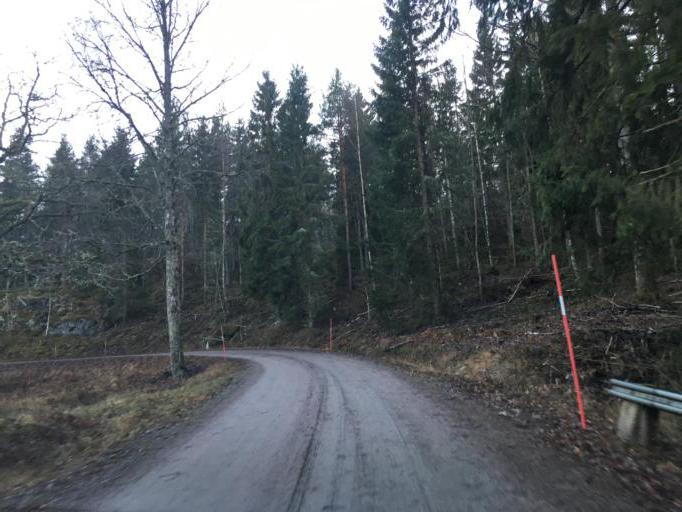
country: SE
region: Kalmar
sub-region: Vasterviks Kommun
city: Vaestervik
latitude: 57.6210
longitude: 16.5163
